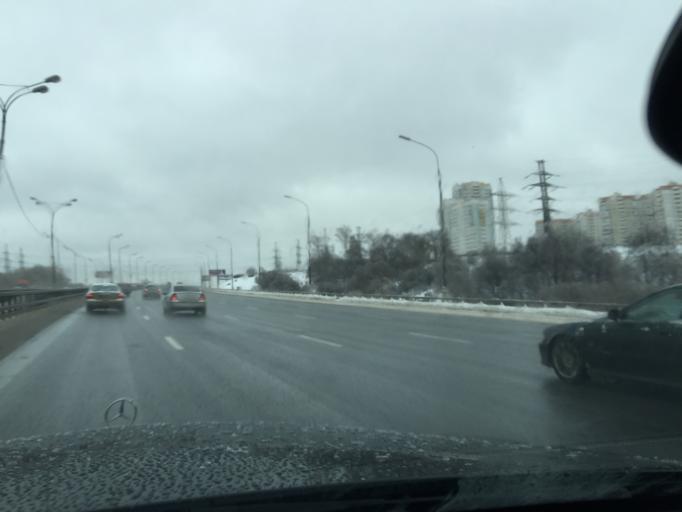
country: RU
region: Moscow
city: Strogino
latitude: 55.8421
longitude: 37.3939
